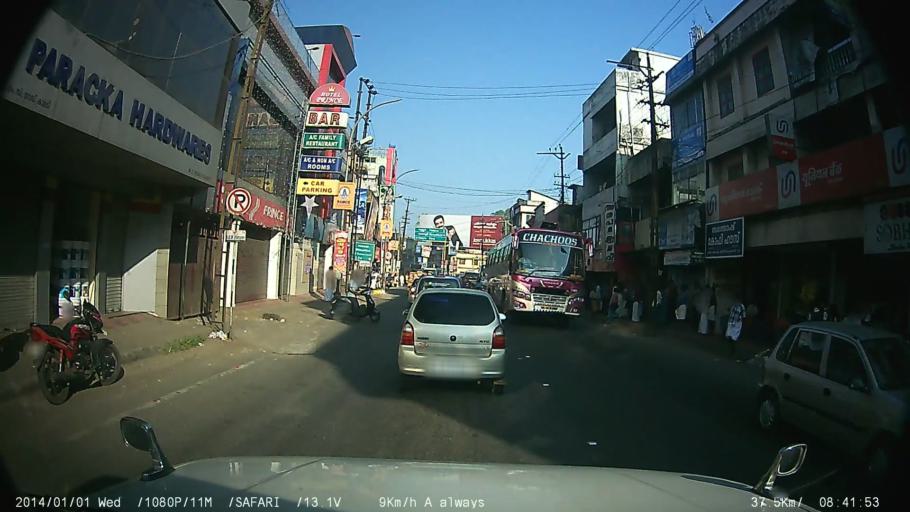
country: IN
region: Kerala
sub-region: Ernakulam
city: Angamali
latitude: 10.1652
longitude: 76.4393
